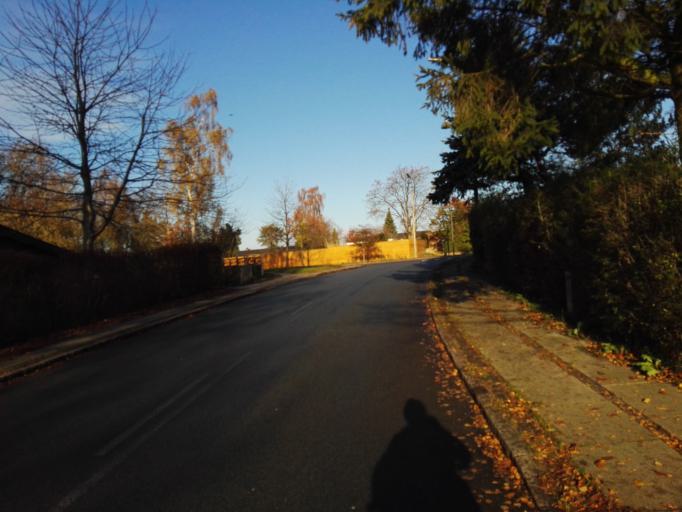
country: DK
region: Capital Region
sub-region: Herlev Kommune
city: Herlev
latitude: 55.7282
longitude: 12.4123
